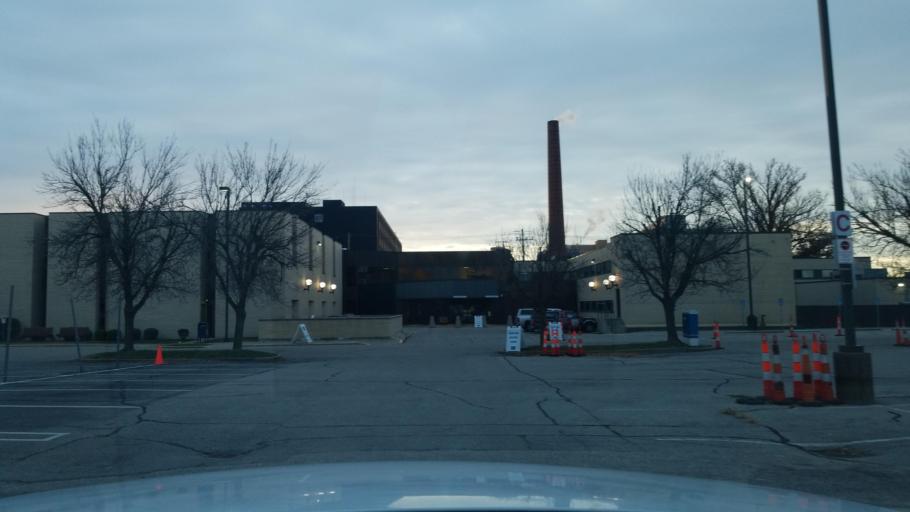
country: US
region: Indiana
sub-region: Vanderburgh County
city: Evansville
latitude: 37.9696
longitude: -87.5680
